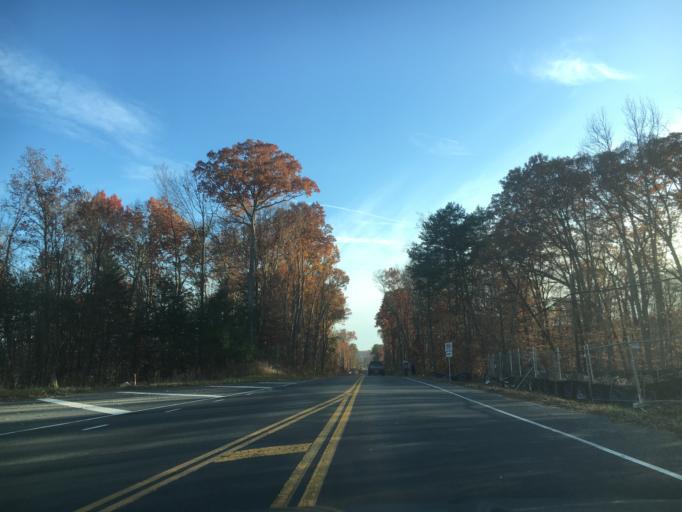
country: US
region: Virginia
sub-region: Prince William County
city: Dumfries
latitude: 38.5802
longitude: -77.3308
